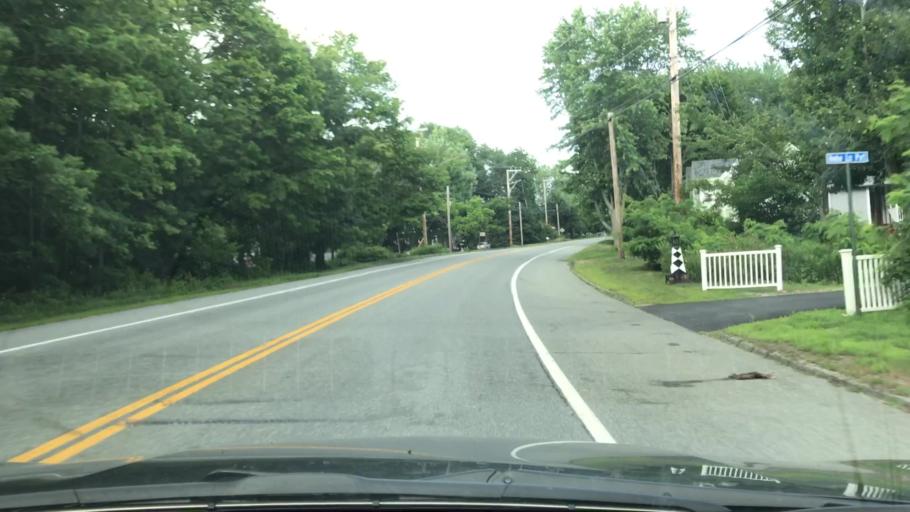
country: US
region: Maine
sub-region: Hancock County
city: Trenton
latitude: 44.4327
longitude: -68.3204
